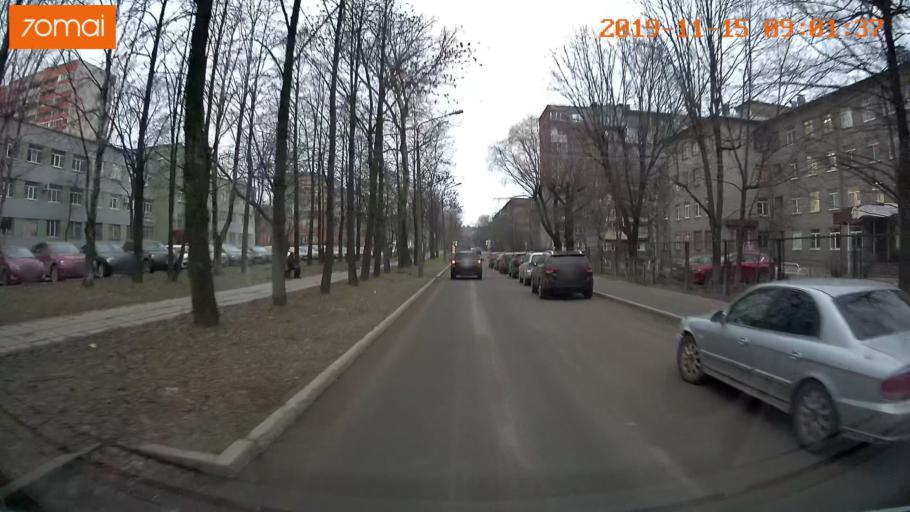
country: RU
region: Vologda
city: Cherepovets
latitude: 59.1332
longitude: 37.9263
